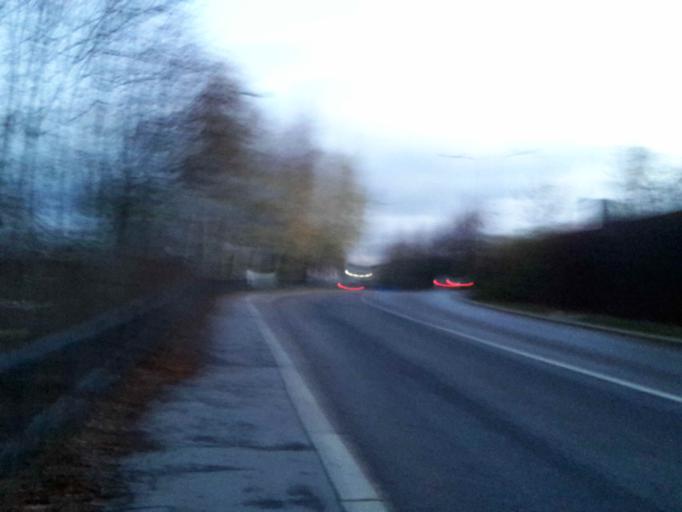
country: CZ
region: Liberecky
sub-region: Okres Liberec
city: Liberec
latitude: 50.7682
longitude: 15.0426
